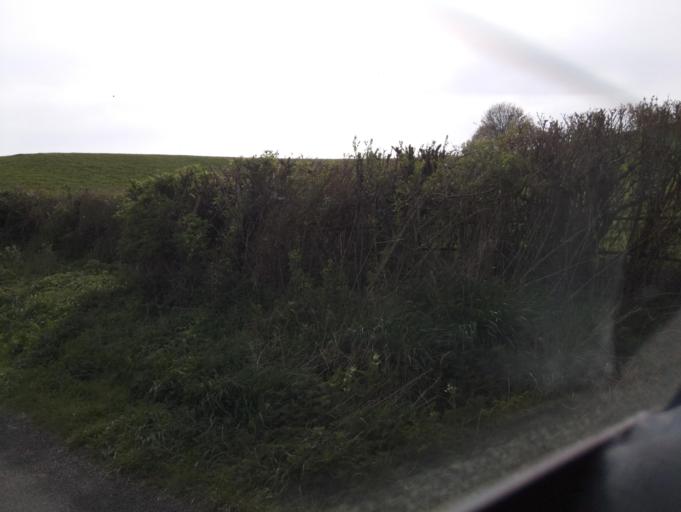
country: GB
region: England
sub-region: Somerset
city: Milborne Port
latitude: 50.9722
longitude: -2.4934
